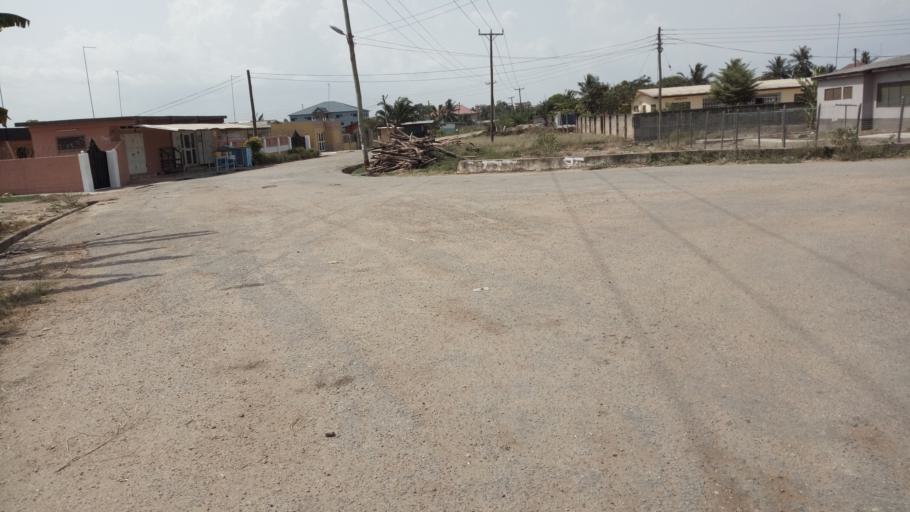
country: GH
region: Central
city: Winneba
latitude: 5.3602
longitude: -0.6355
